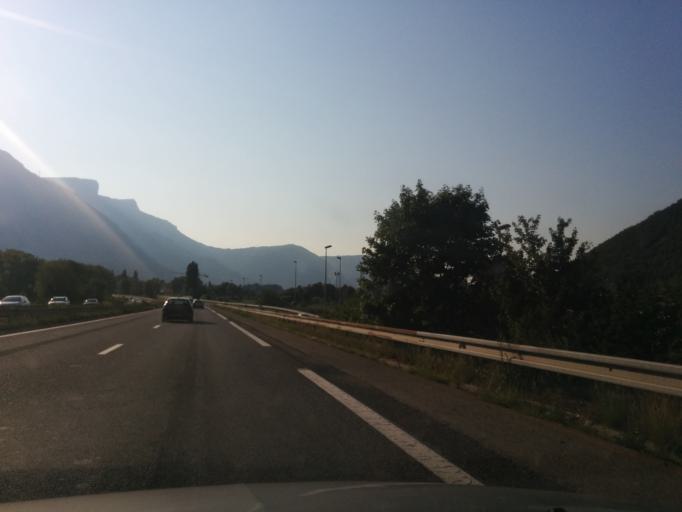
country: FR
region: Rhone-Alpes
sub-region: Departement de l'Isere
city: Saint-Martin-le-Vinoux
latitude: 45.2087
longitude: 5.7018
